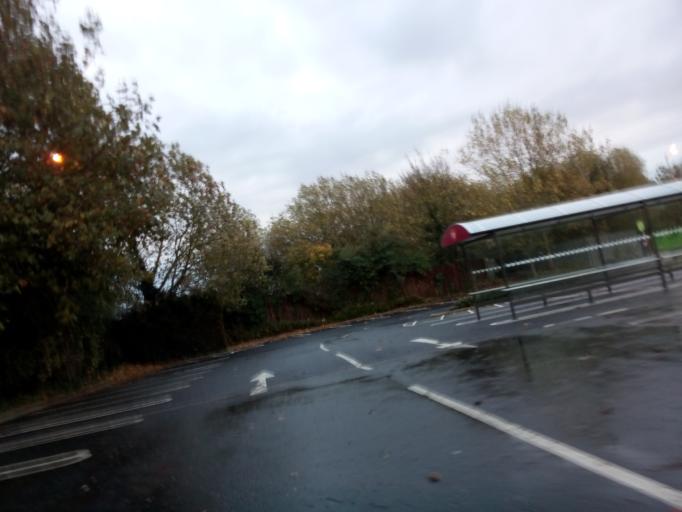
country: GB
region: England
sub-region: Suffolk
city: Ipswich
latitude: 52.0597
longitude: 1.1336
